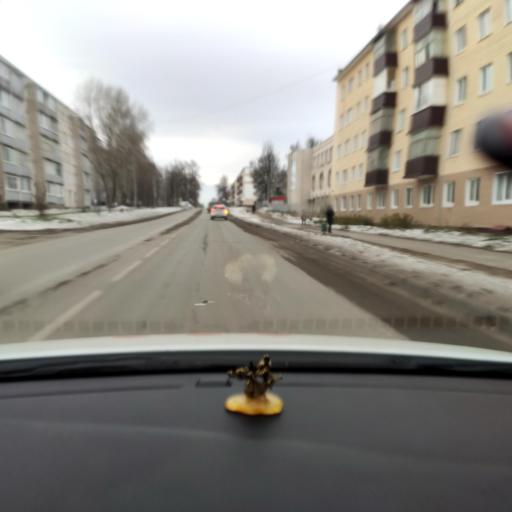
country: RU
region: Tatarstan
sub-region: Zelenodol'skiy Rayon
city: Zelenodolsk
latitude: 55.8495
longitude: 48.5213
